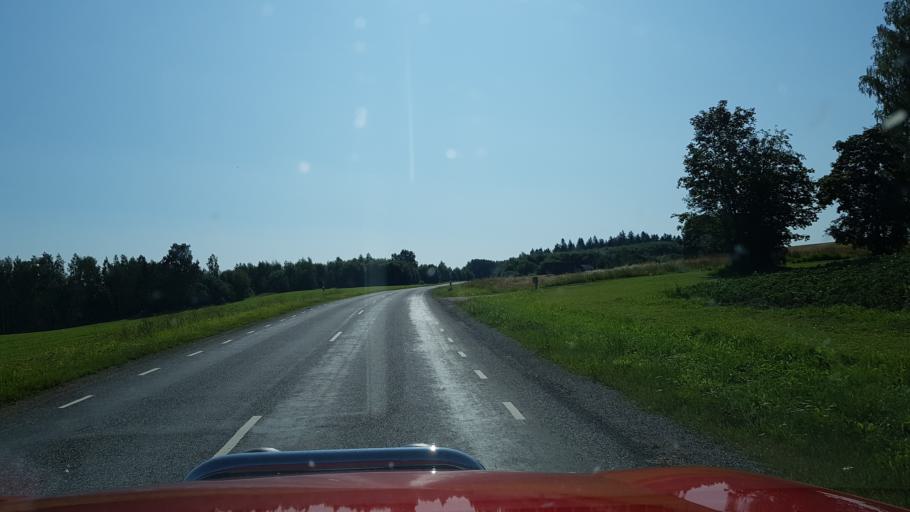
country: EE
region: Vorumaa
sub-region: Voru linn
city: Voru
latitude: 57.9762
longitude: 26.8203
